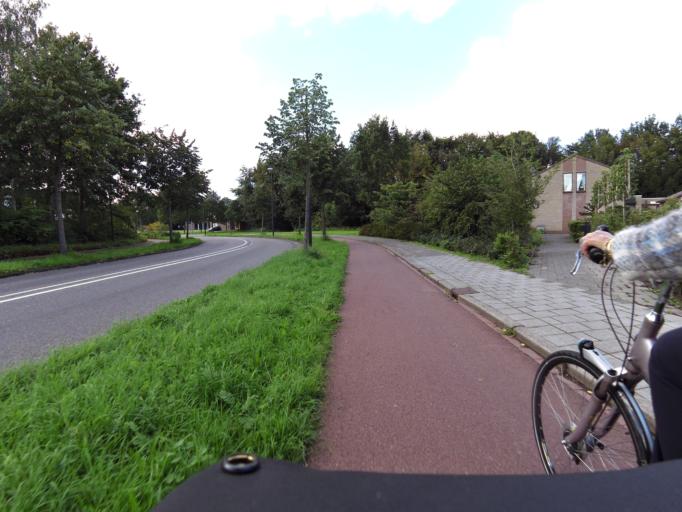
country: NL
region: South Holland
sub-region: Gemeente Vlaardingen
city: Vlaardingen
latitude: 51.9381
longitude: 4.3396
